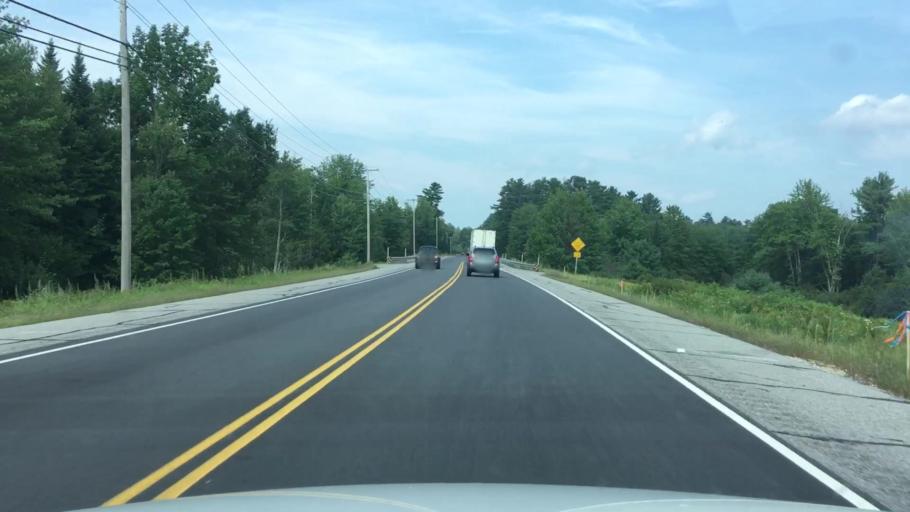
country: US
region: Maine
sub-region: Androscoggin County
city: Turner
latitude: 44.2247
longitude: -70.2499
